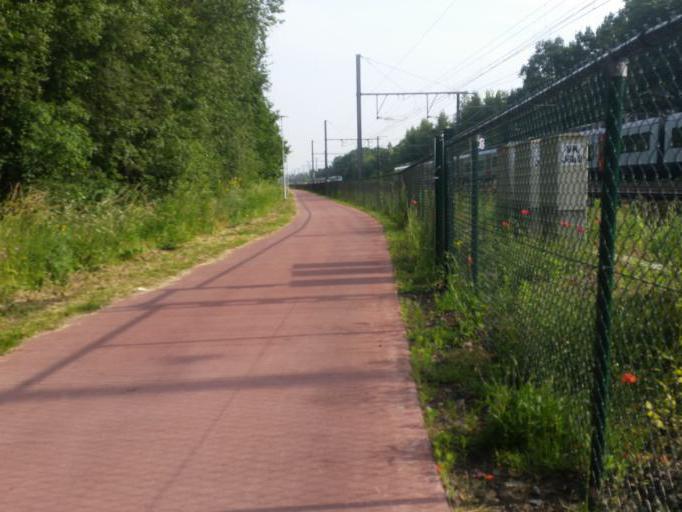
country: BE
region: Flanders
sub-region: Provincie Antwerpen
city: Duffel
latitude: 51.0782
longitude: 4.4962
